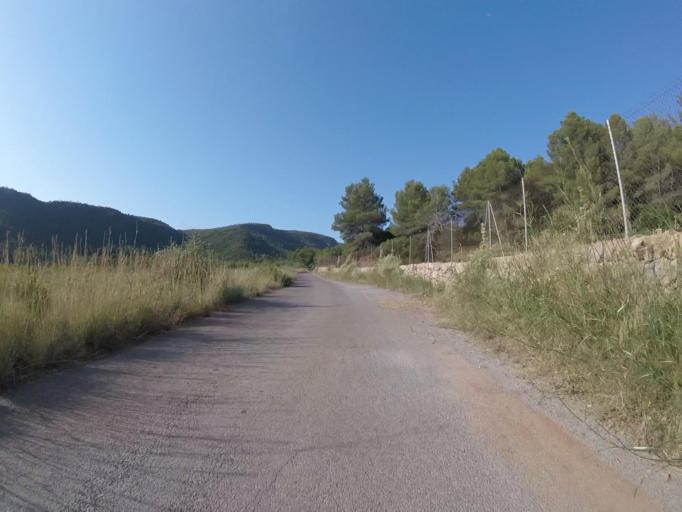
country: ES
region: Valencia
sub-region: Provincia de Castello
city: Benicassim
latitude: 40.1031
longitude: 0.0645
